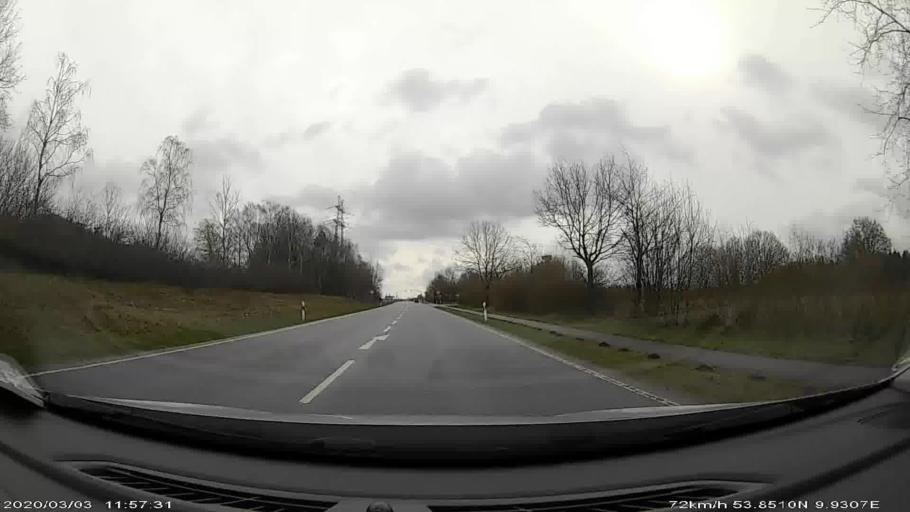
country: DE
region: Schleswig-Holstein
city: Nutzen
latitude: 53.8500
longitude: 9.9327
